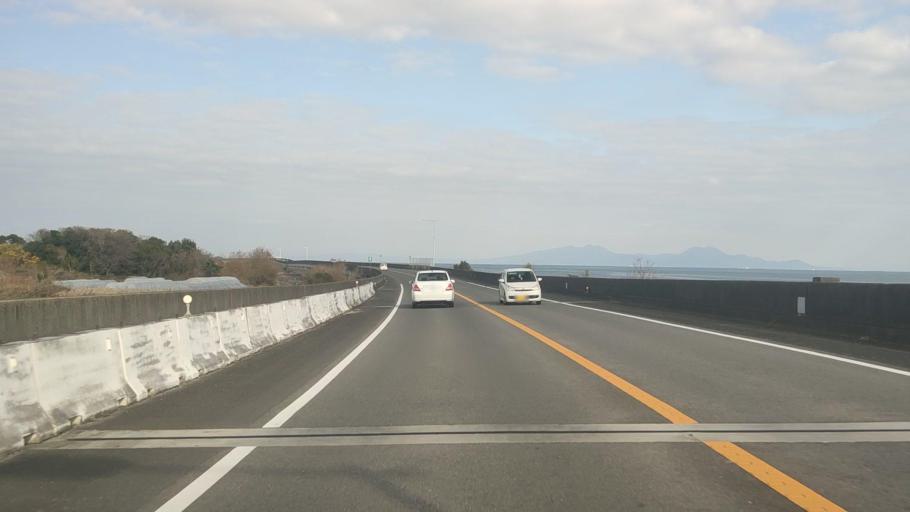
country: JP
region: Nagasaki
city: Shimabara
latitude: 32.7221
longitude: 130.3589
